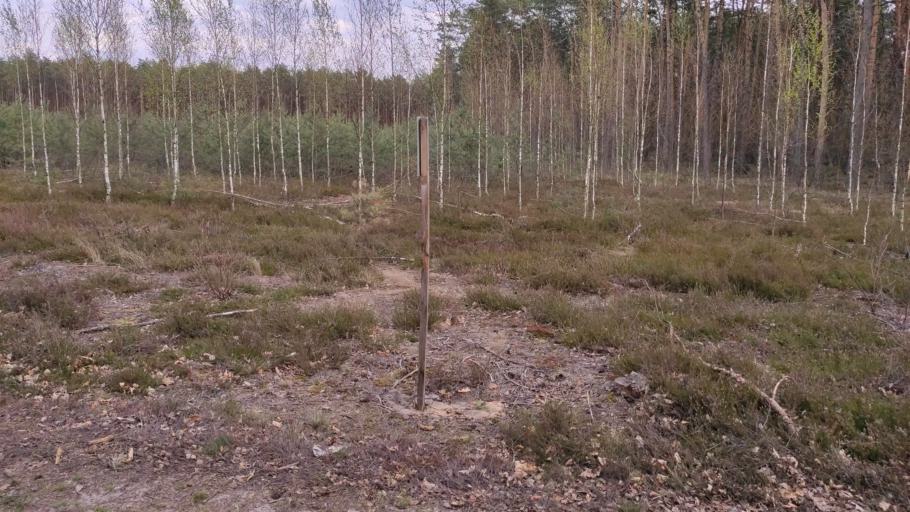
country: PL
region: Masovian Voivodeship
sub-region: Powiat grojecki
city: Warka
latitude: 51.7602
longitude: 21.1930
